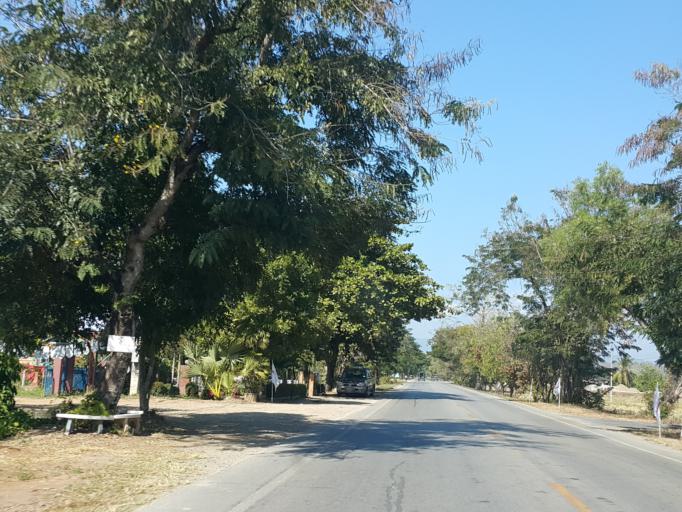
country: TH
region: Chiang Mai
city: Mae Taeng
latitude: 19.0531
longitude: 98.9609
